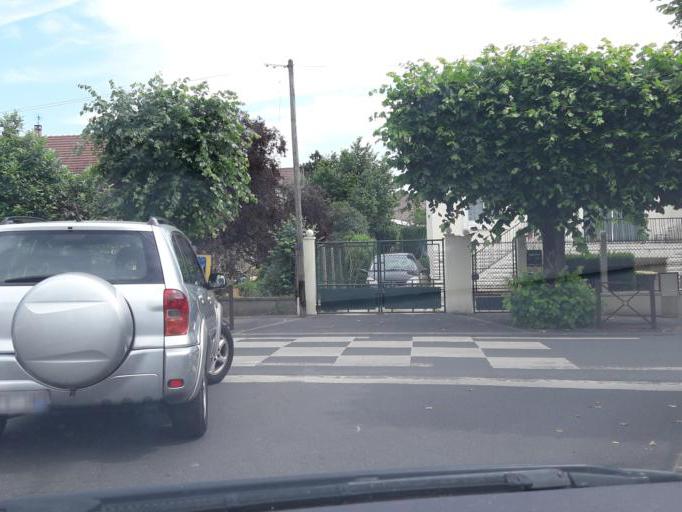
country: FR
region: Ile-de-France
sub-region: Departement de l'Essonne
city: Morsang-sur-Orge
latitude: 48.6524
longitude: 2.3486
